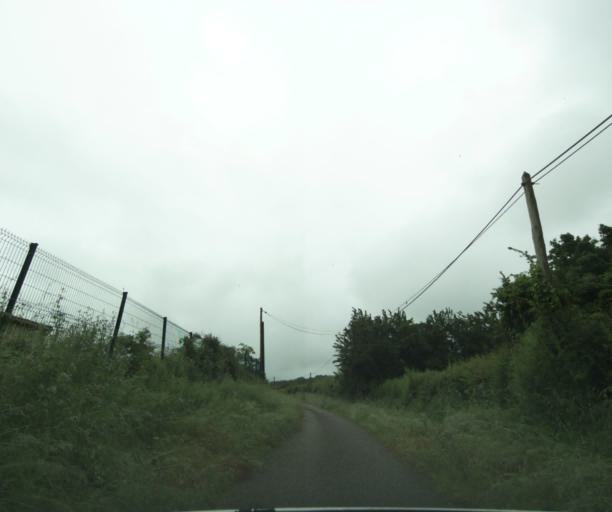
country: FR
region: Bourgogne
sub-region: Departement de Saone-et-Loire
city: Charolles
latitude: 46.4384
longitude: 4.3212
